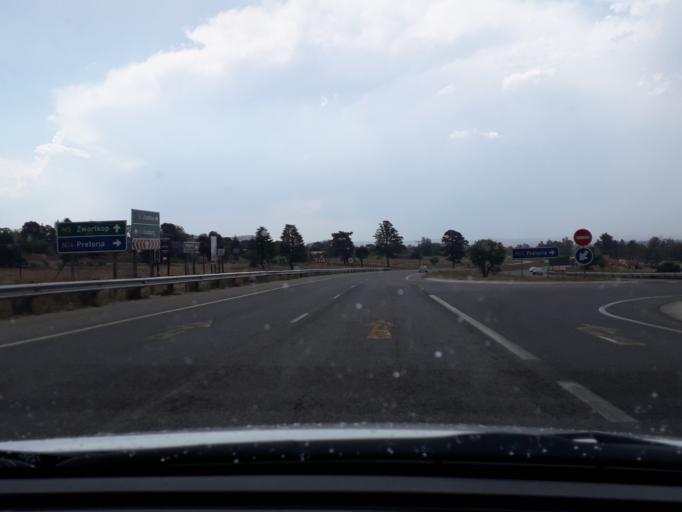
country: ZA
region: Gauteng
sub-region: West Rand District Municipality
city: Muldersdriseloop
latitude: -26.0189
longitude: 27.8596
